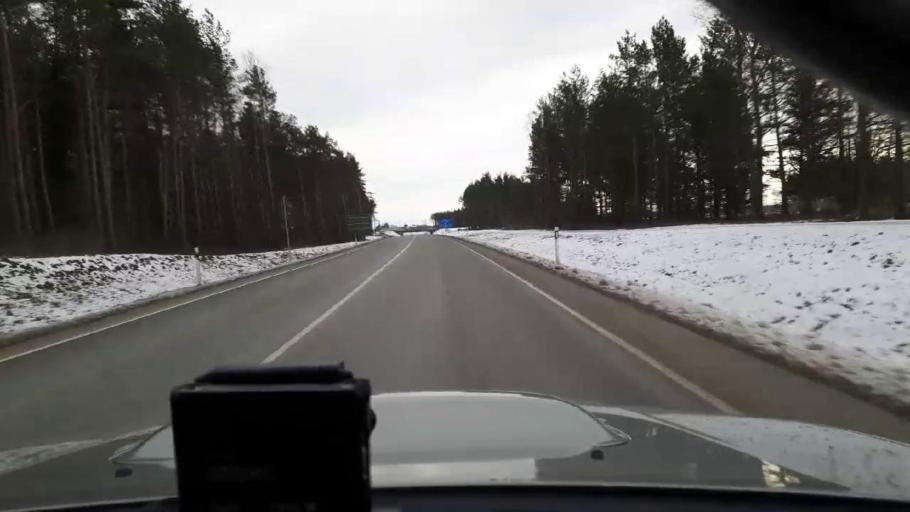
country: EE
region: Harju
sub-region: Saue vald
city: Laagri
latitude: 59.3451
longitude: 24.6018
